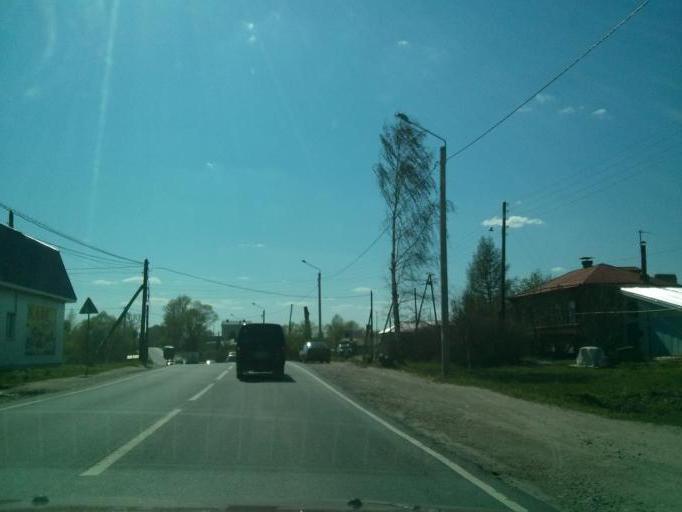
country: RU
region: Nizjnij Novgorod
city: Vorsma
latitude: 56.0377
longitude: 43.3700
